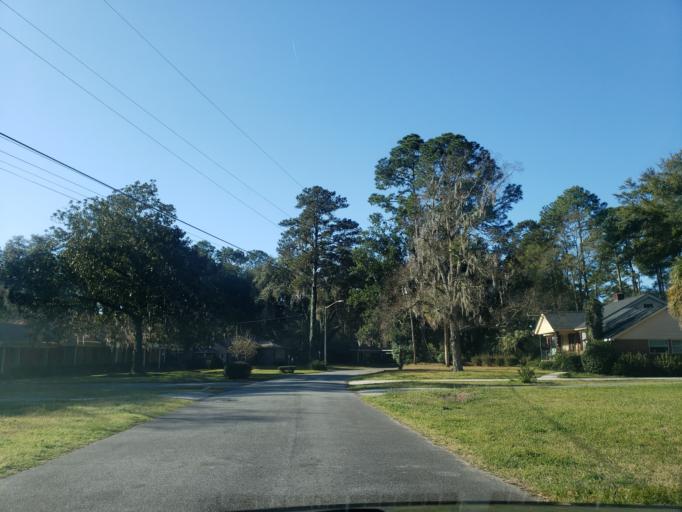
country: US
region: Georgia
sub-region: Chatham County
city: Thunderbolt
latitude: 32.0203
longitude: -81.0914
